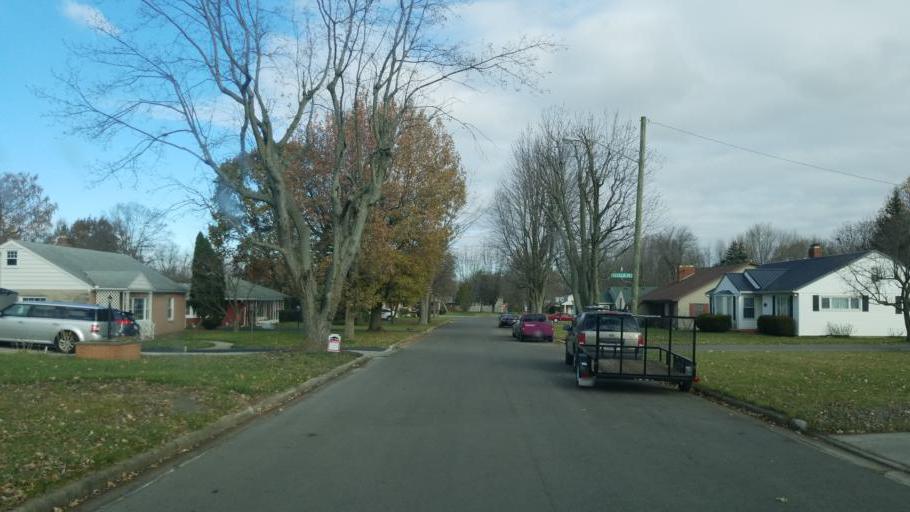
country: US
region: Ohio
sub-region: Hardin County
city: Kenton
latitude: 40.6563
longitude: -83.6040
